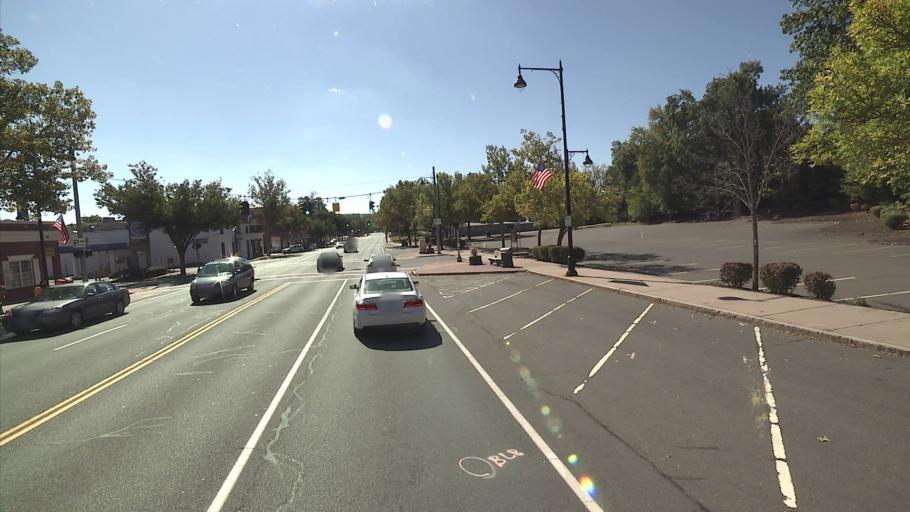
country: US
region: Connecticut
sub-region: Hartford County
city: Manchester
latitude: 41.7684
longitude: -72.5207
